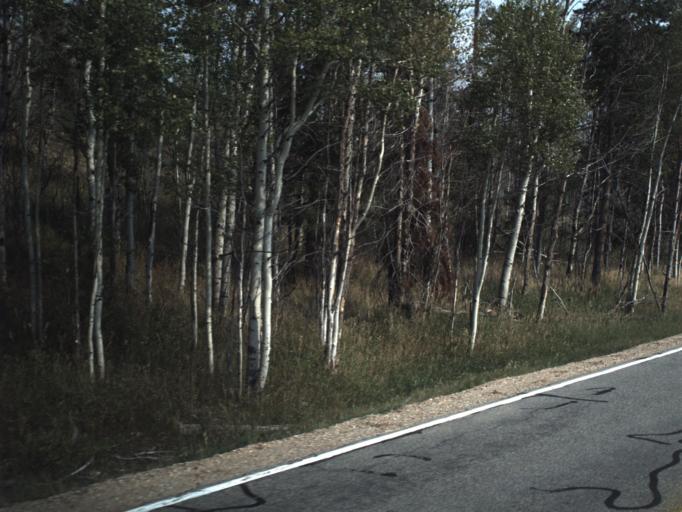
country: US
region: Utah
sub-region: Summit County
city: Francis
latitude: 40.6046
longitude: -111.1194
